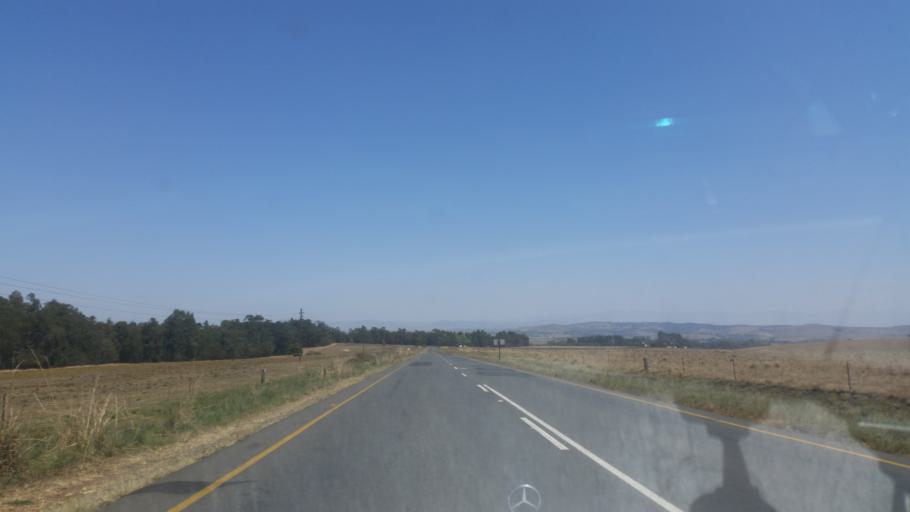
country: ZA
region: KwaZulu-Natal
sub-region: uMgungundlovu District Municipality
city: Mooirivier
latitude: -29.1448
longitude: 29.9919
